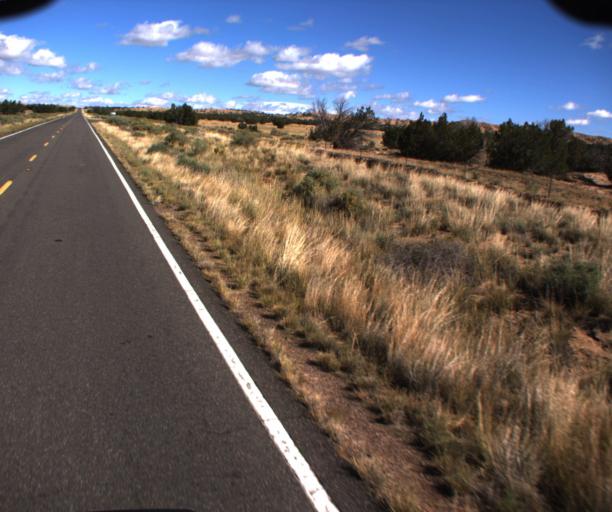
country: US
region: Arizona
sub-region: Apache County
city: Saint Johns
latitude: 34.8045
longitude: -109.2378
